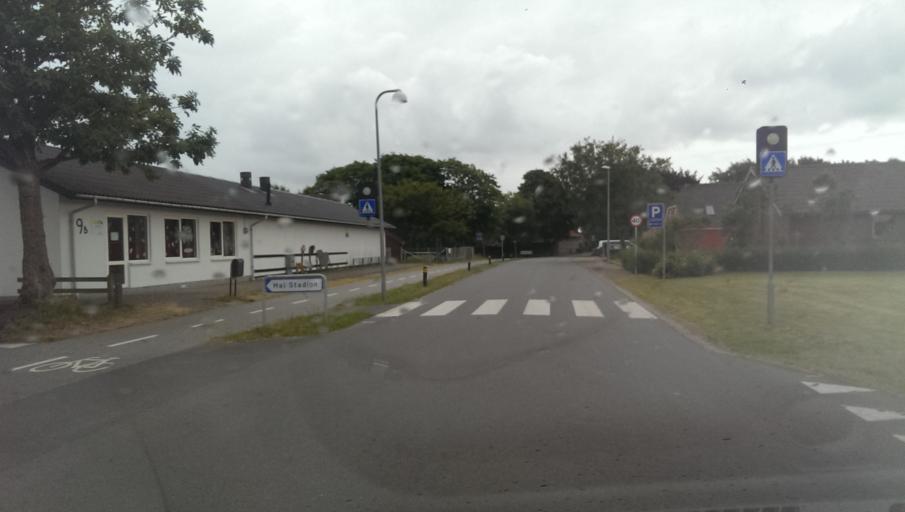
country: DK
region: South Denmark
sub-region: Esbjerg Kommune
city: Bramming
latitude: 55.4373
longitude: 8.7207
